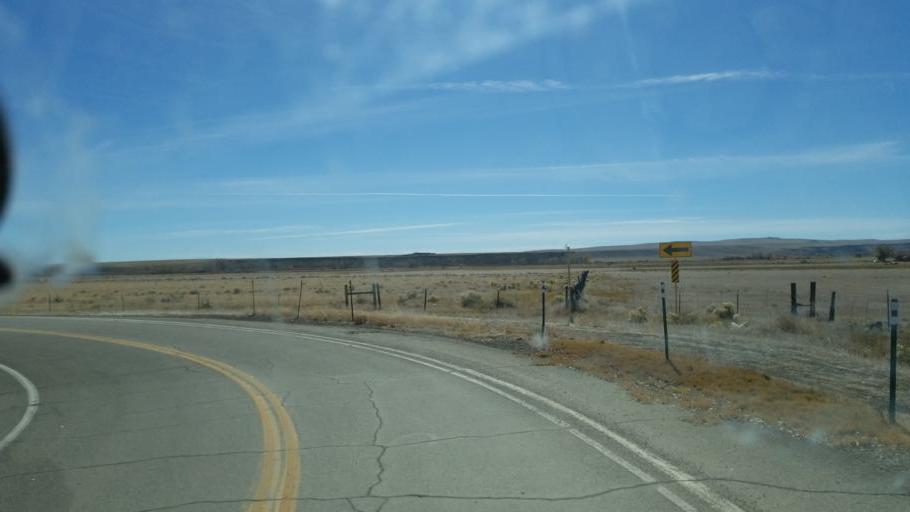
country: US
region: Colorado
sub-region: Conejos County
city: Conejos
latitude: 37.2835
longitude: -106.1479
